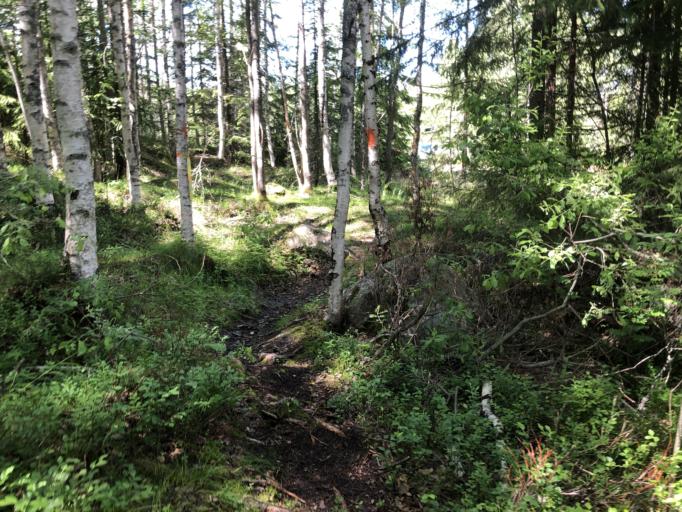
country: SE
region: Dalarna
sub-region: Vansbro Kommun
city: Vansbro
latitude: 60.6701
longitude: 14.2697
